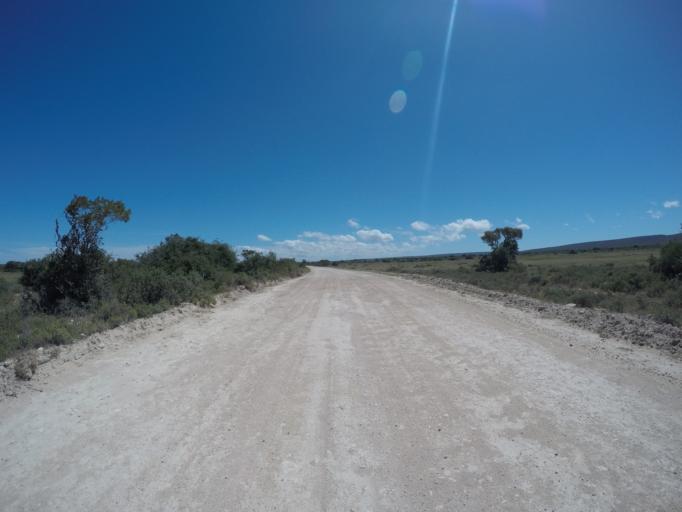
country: ZA
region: Western Cape
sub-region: Overberg District Municipality
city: Bredasdorp
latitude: -34.4547
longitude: 20.4219
